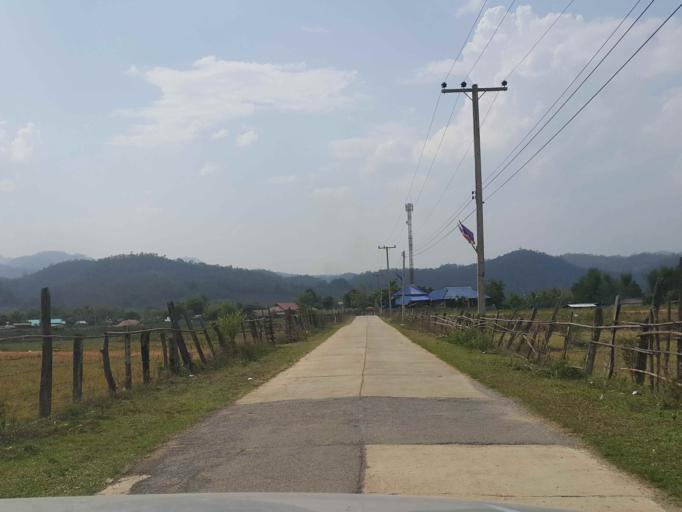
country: TH
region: Chiang Mai
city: Wiang Haeng
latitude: 19.3815
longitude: 98.7186
